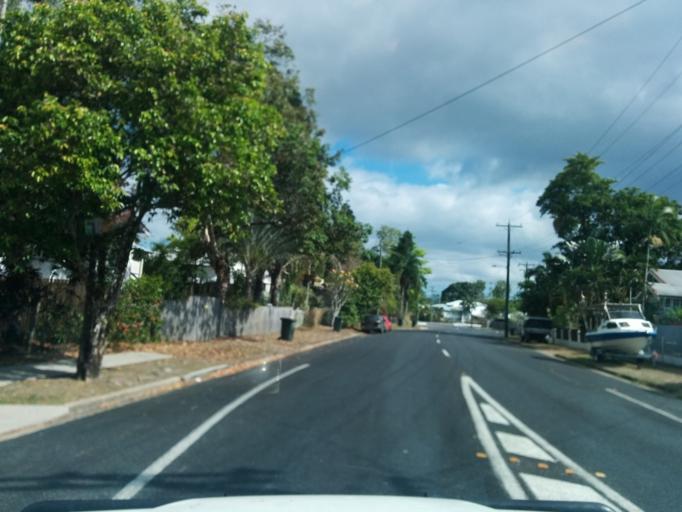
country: AU
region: Queensland
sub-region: Cairns
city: Cairns
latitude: -16.9100
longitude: 145.7561
